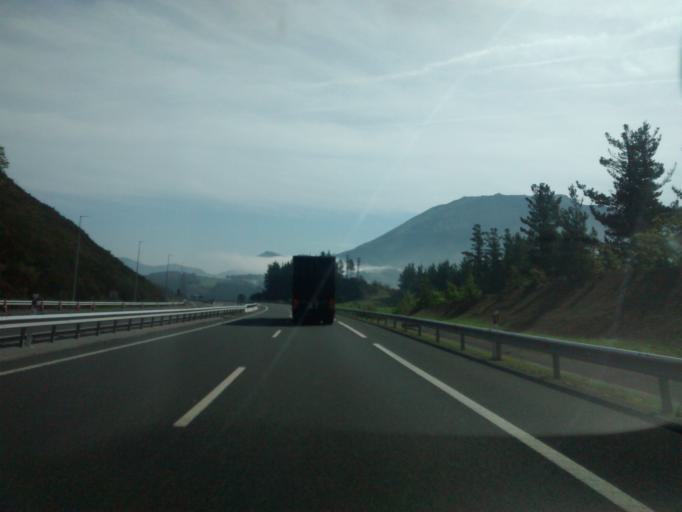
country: ES
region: Basque Country
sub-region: Provincia de Guipuzcoa
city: Eskoriatza
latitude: 43.0167
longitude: -2.5401
